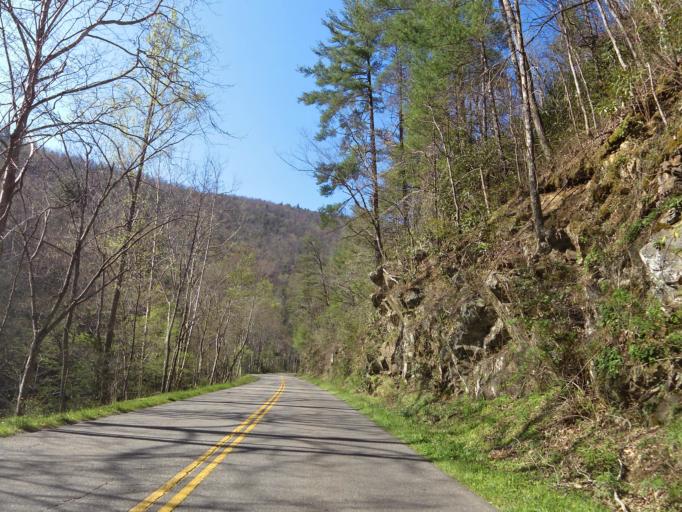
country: US
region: Tennessee
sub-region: Sevier County
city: Gatlinburg
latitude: 35.6671
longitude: -83.6276
